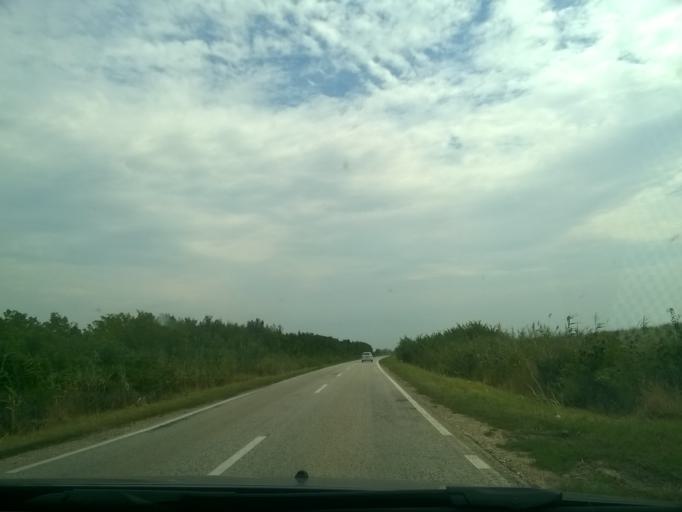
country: RS
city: Banatski Despotovac
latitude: 45.3871
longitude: 20.6236
